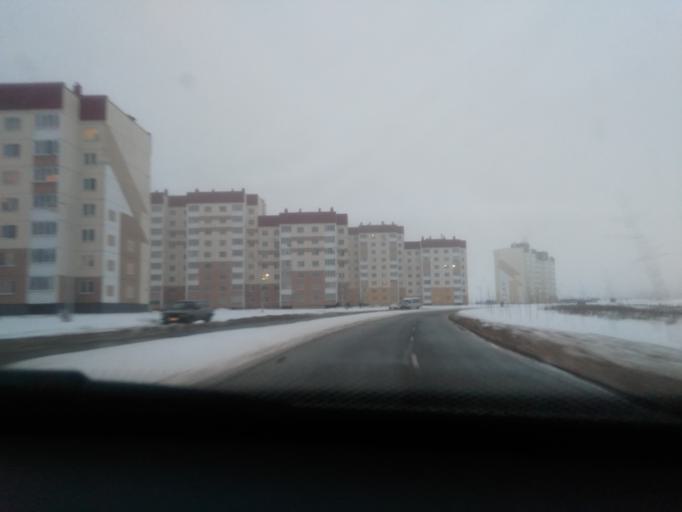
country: BY
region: Mogilev
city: Babruysk
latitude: 53.2005
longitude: 29.2239
